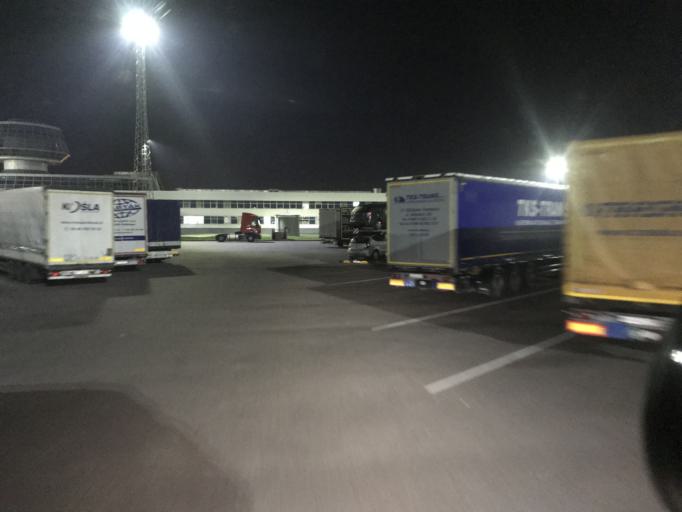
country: PL
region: Lublin Voivodeship
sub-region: Powiat bialski
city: Terespol
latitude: 52.1224
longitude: 23.5732
